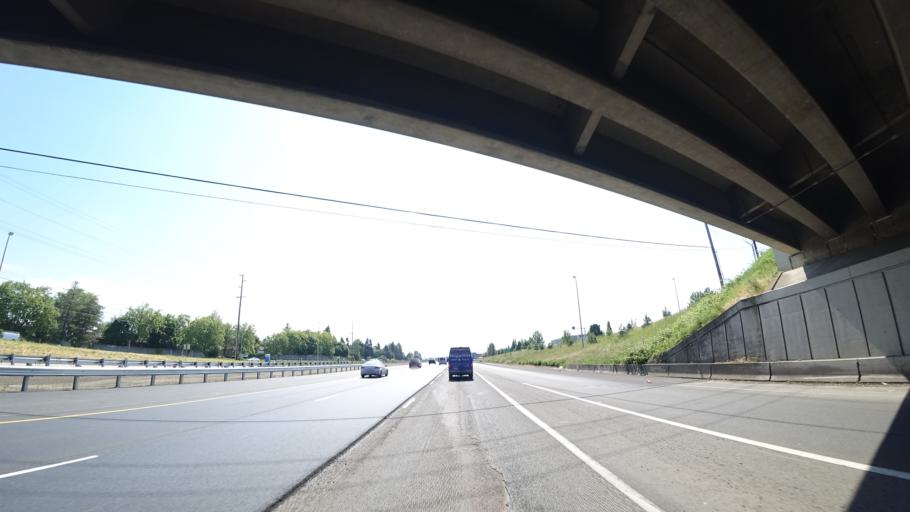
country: US
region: Oregon
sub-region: Washington County
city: Rockcreek
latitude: 45.5417
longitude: -122.8677
